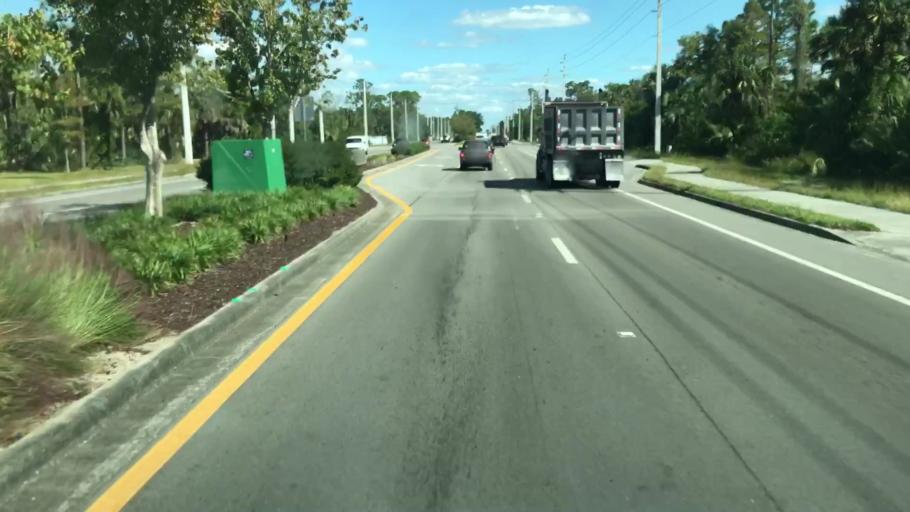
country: US
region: Florida
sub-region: Collier County
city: Vineyards
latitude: 26.2293
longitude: -81.6461
